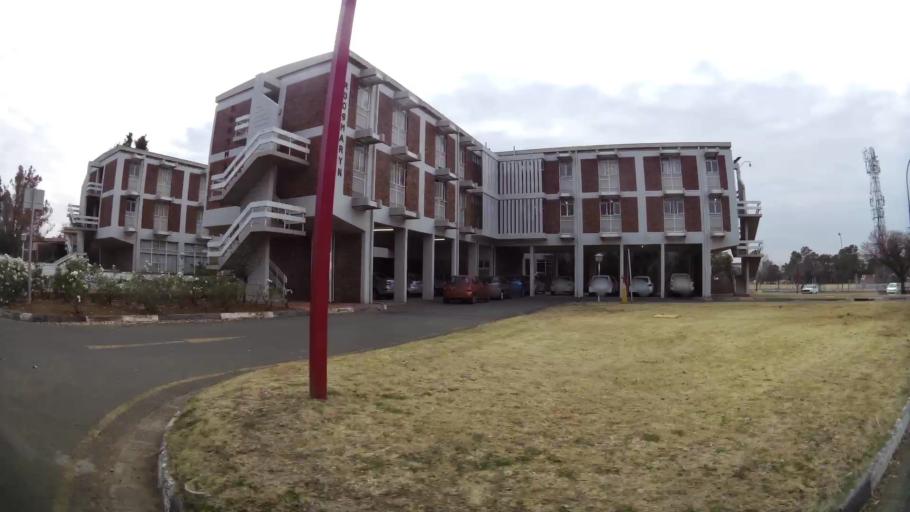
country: ZA
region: Orange Free State
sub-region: Mangaung Metropolitan Municipality
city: Bloemfontein
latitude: -29.1160
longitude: 26.1898
